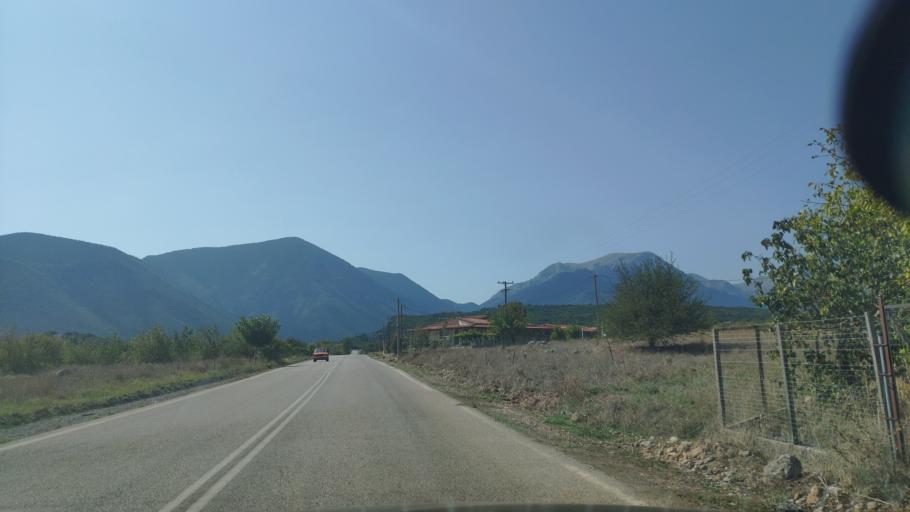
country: GR
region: Peloponnese
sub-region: Nomos Korinthias
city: Nemea
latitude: 37.8664
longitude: 22.4570
